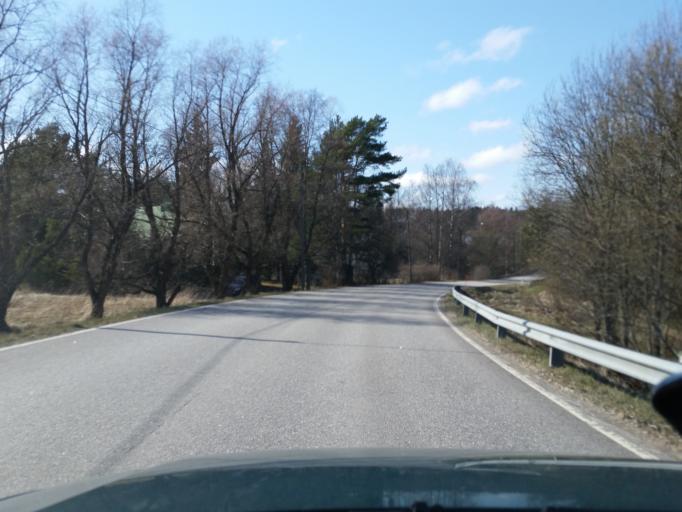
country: FI
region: Uusimaa
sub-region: Helsinki
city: Karkkila
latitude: 60.4335
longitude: 24.2051
